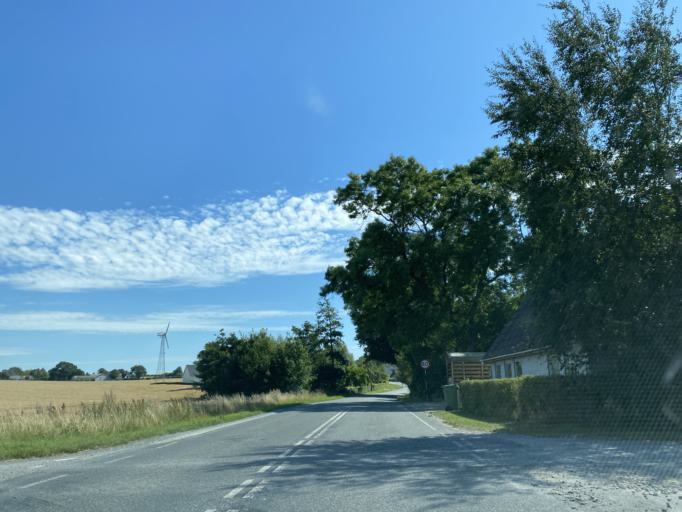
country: DK
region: South Denmark
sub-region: Faaborg-Midtfyn Kommune
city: Ringe
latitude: 55.2092
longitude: 10.3776
